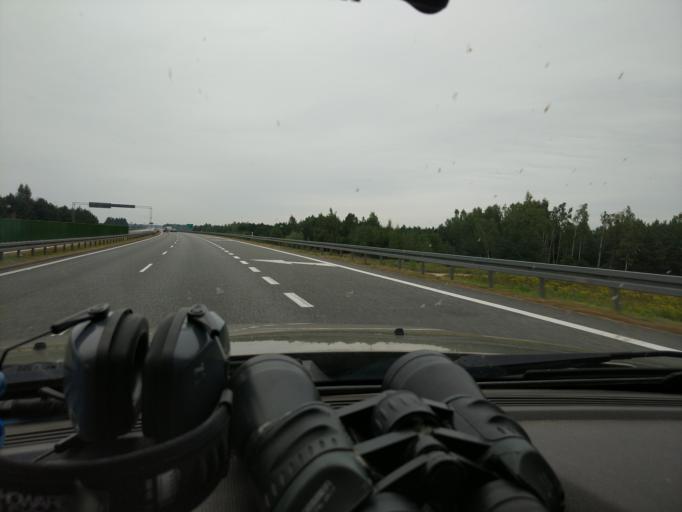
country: PL
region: Masovian Voivodeship
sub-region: Powiat wyszkowski
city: Wyszkow
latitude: 52.5892
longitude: 21.4989
